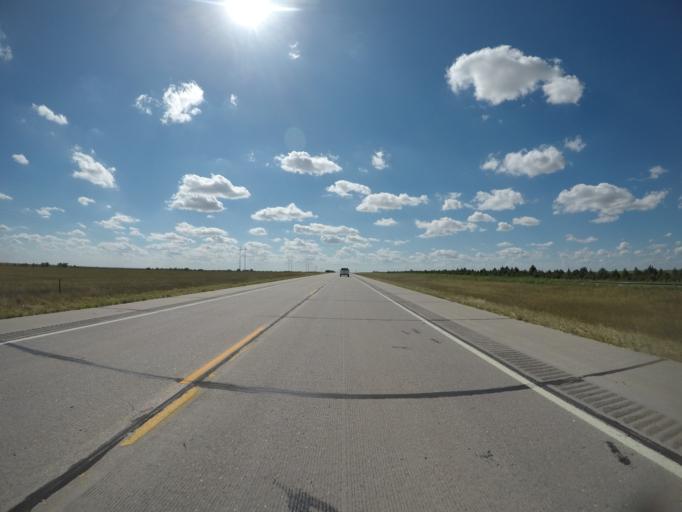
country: US
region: Colorado
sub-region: Phillips County
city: Holyoke
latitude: 40.5975
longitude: -102.3832
